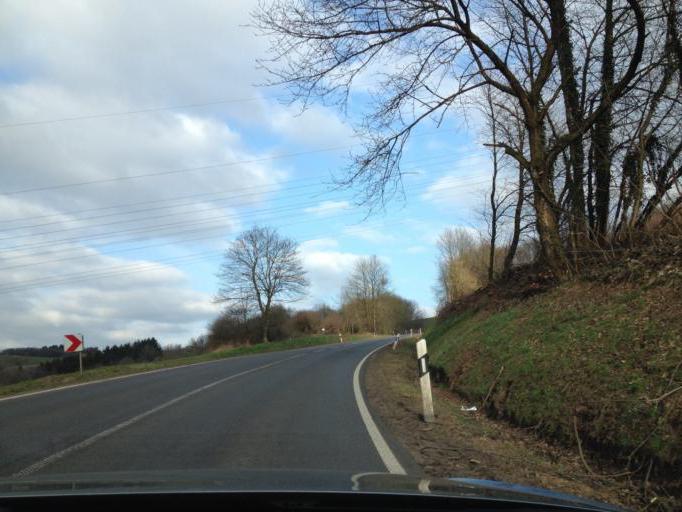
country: DE
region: Saarland
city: Marpingen
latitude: 49.4737
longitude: 7.0758
